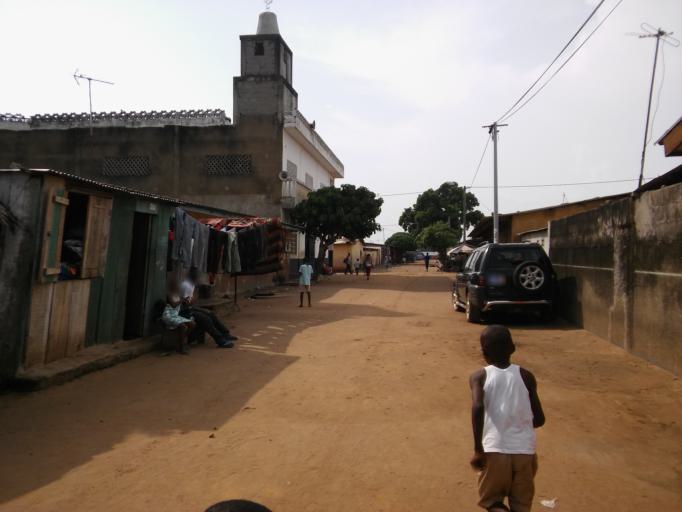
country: CI
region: Sud-Comoe
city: Grand-Bassam
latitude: 5.2067
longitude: -3.7332
